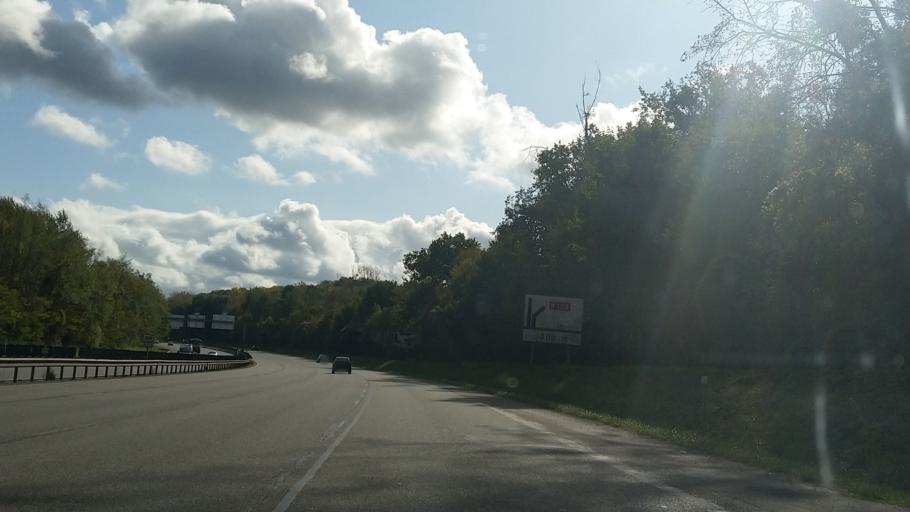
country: FR
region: Ile-de-France
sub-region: Departement du Val-d'Oise
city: Mours
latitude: 49.1188
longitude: 2.2524
